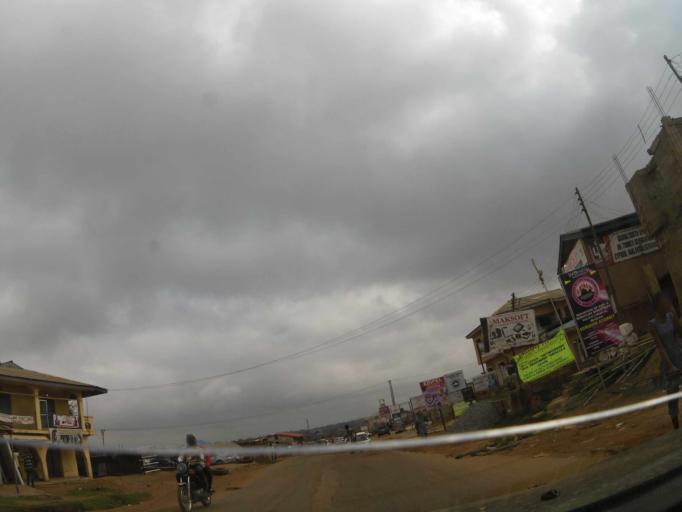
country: NG
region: Oyo
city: Ibadan
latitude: 7.4424
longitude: 3.9515
